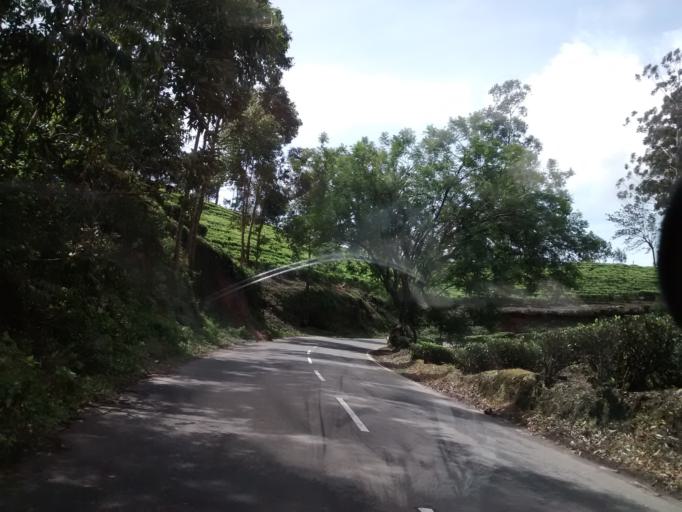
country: IN
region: Kerala
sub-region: Idukki
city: Munnar
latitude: 10.0918
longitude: 77.0876
